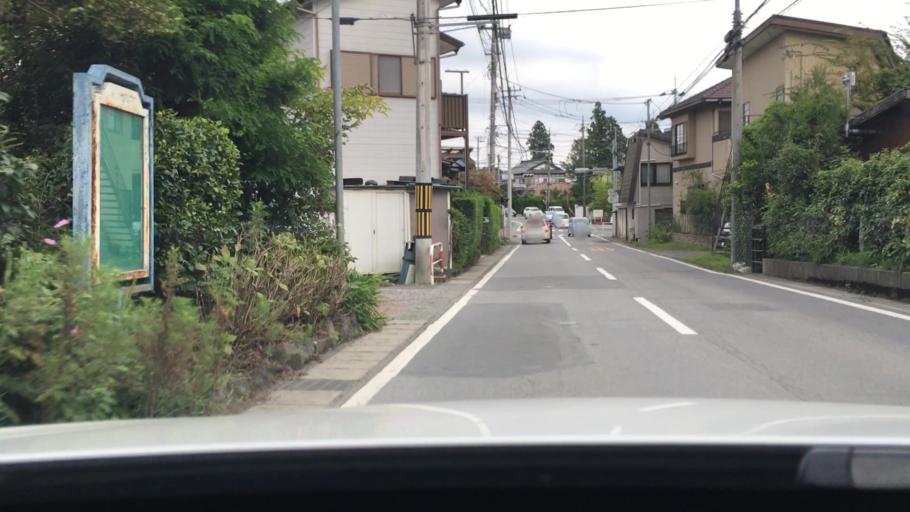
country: JP
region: Shizuoka
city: Gotemba
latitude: 35.3232
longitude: 138.9089
